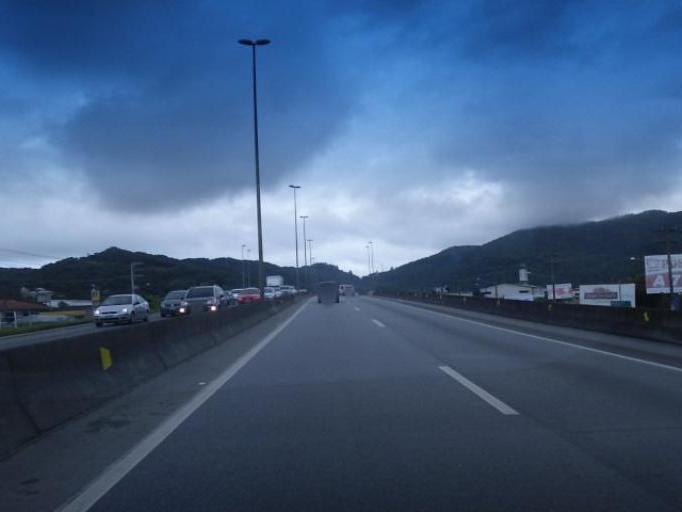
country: BR
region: Santa Catarina
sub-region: Balneario Camboriu
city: Balneario Camboriu
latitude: -27.0177
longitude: -48.6108
